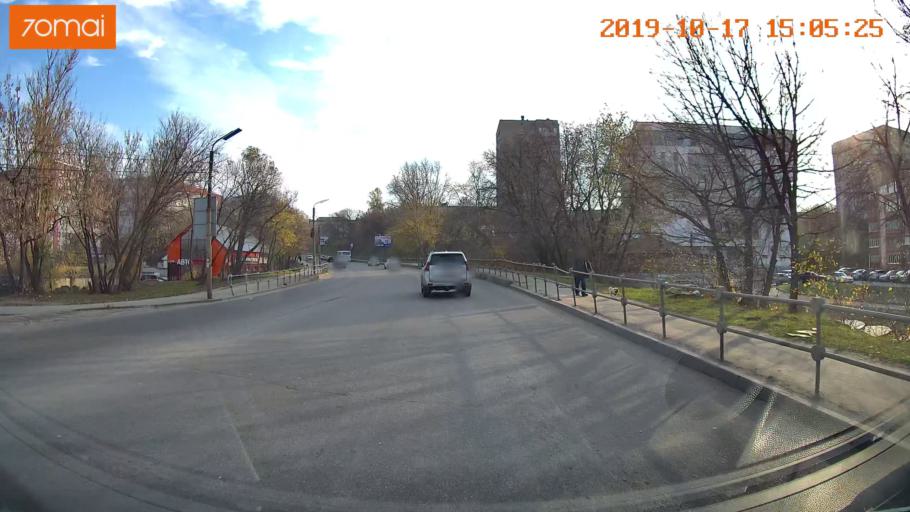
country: RU
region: Rjazan
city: Ryazan'
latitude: 54.6363
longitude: 39.7231
